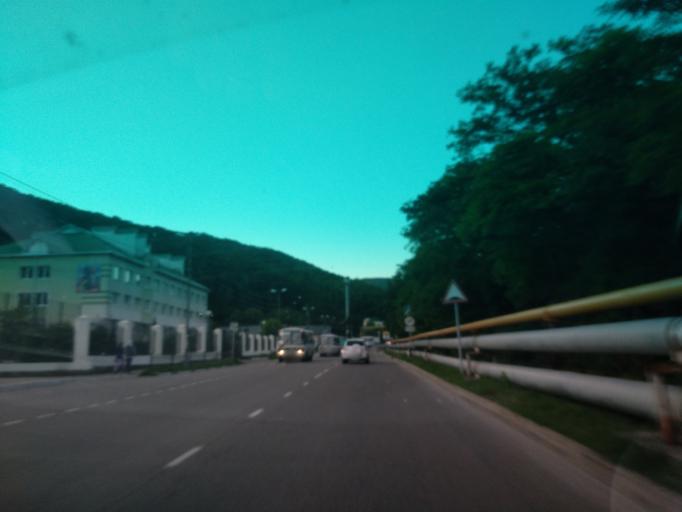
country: RU
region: Krasnodarskiy
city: Tuapse
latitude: 44.1197
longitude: 39.0698
